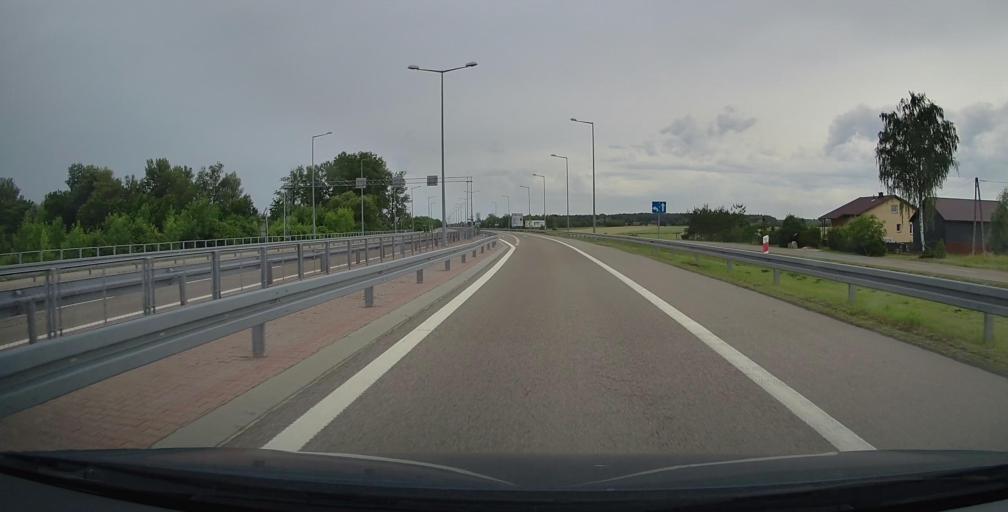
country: PL
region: Lublin Voivodeship
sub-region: Powiat bialski
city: Terespol
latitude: 52.0670
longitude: 23.6360
